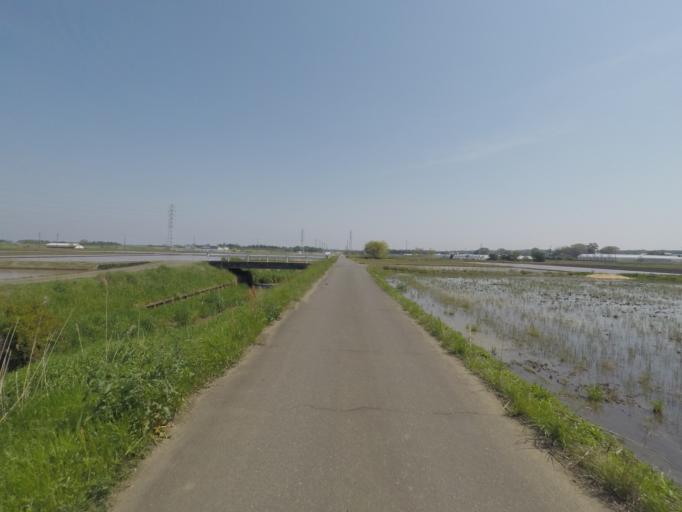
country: JP
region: Ibaraki
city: Naka
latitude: 36.1007
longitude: 140.1589
